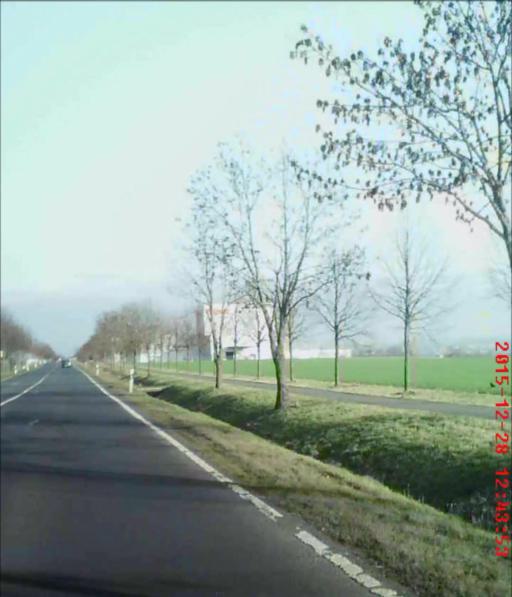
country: DE
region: Thuringia
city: Wiegendorf
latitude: 50.9999
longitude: 11.4472
